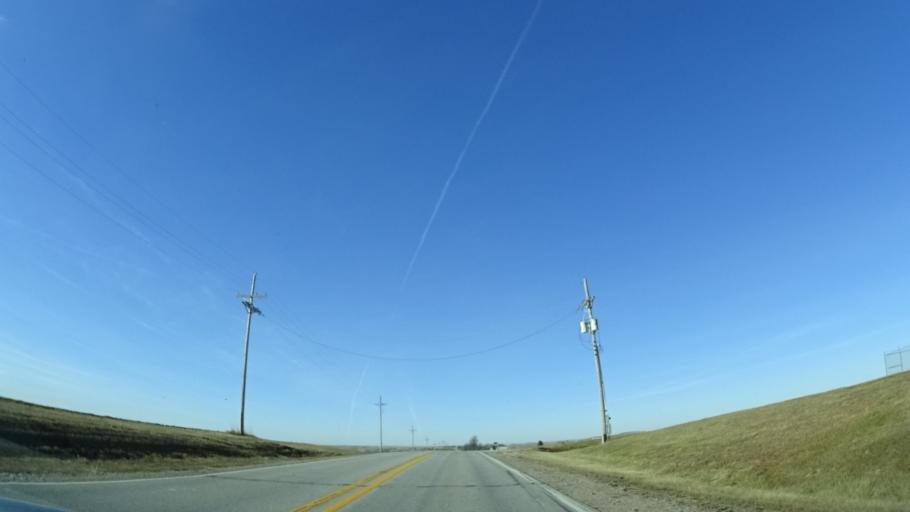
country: US
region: Nebraska
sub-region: Sarpy County
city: Springfield
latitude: 41.0890
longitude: -96.1155
